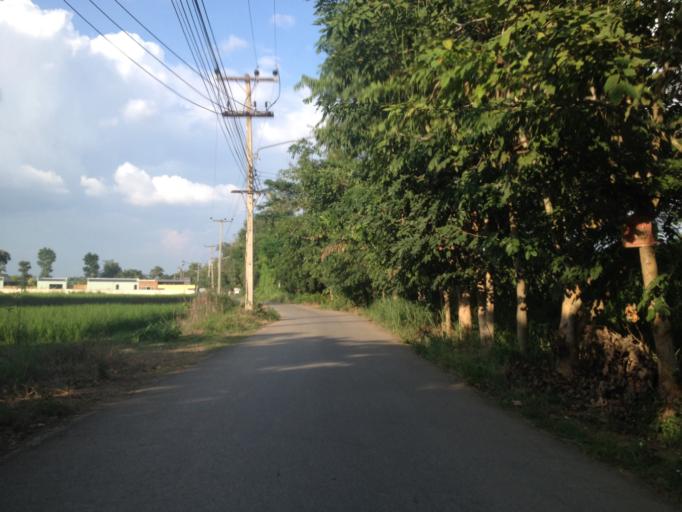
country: TH
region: Chiang Mai
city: Hang Dong
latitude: 18.6977
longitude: 98.9065
